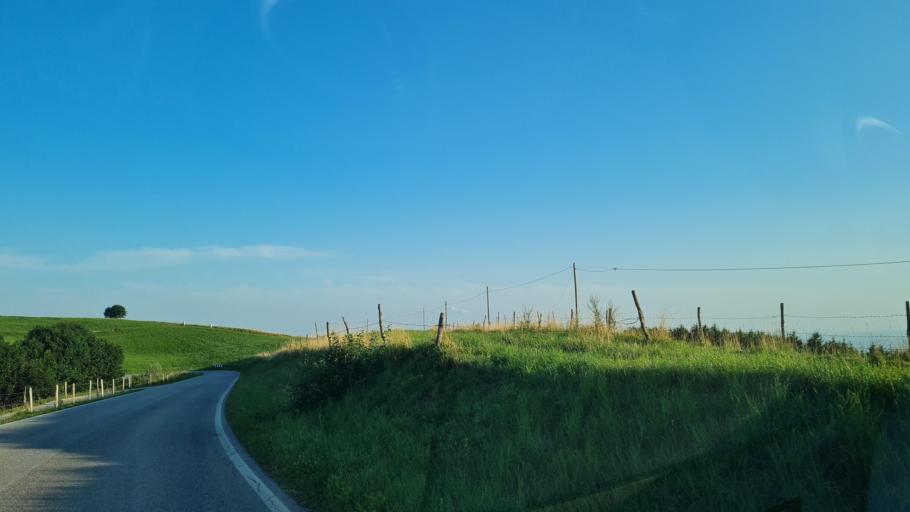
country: IT
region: Veneto
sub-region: Provincia di Vicenza
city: Conco
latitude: 45.8056
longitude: 11.6478
